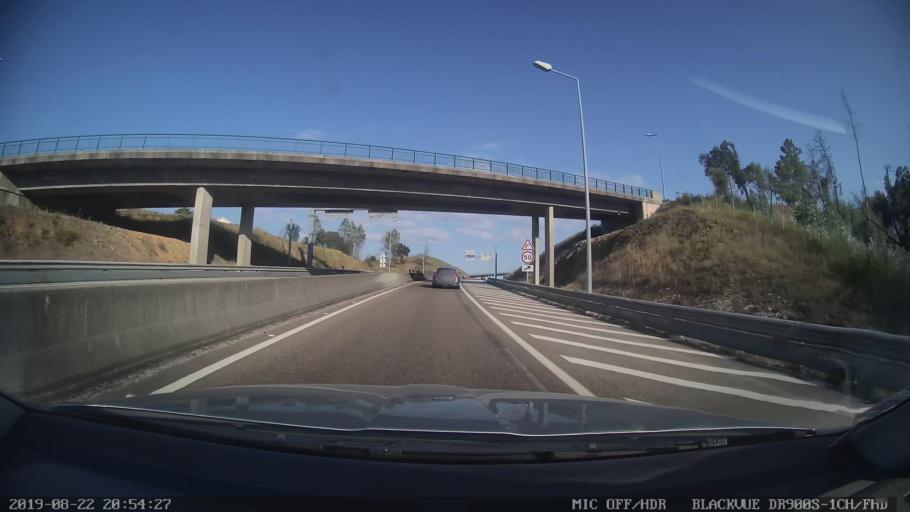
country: PT
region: Castelo Branco
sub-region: Serta
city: Serta
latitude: 39.7735
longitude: -8.0142
